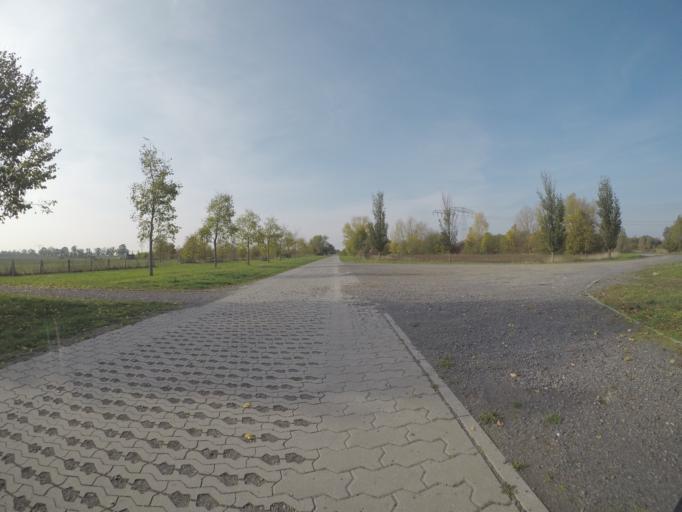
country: DE
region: Brandenburg
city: Schonefeld
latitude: 52.3932
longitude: 13.4880
